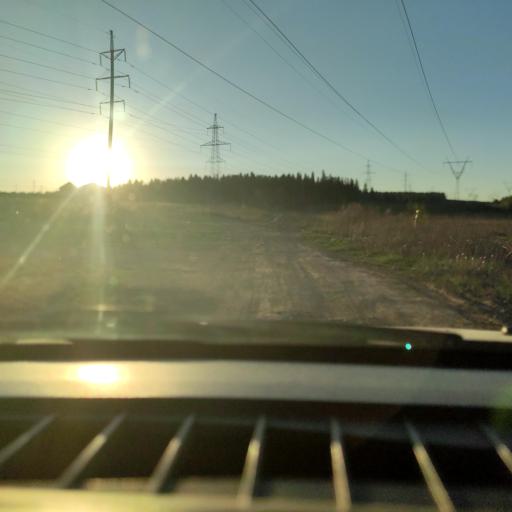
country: RU
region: Perm
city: Ferma
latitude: 57.9517
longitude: 56.3632
